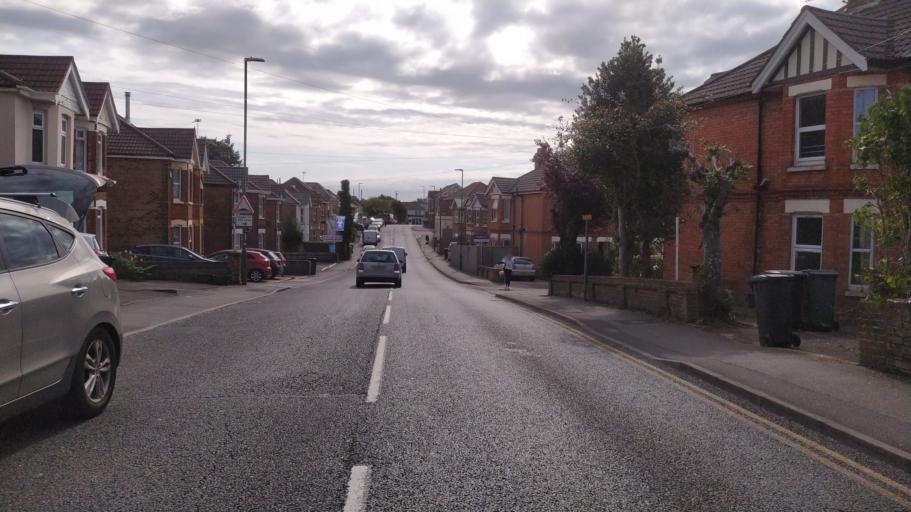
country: GB
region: England
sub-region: Bournemouth
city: Bournemouth
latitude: 50.7434
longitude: -1.8826
